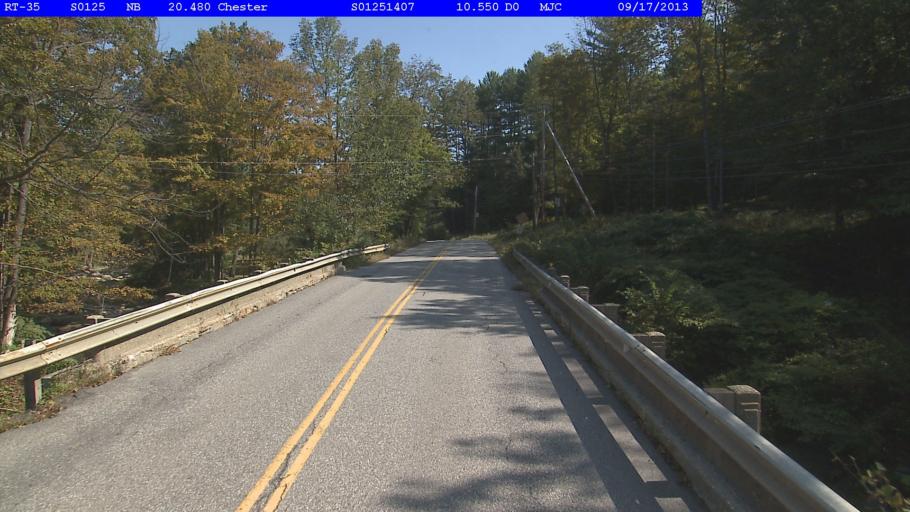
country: US
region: Vermont
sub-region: Windsor County
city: Chester
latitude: 43.2550
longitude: -72.6020
